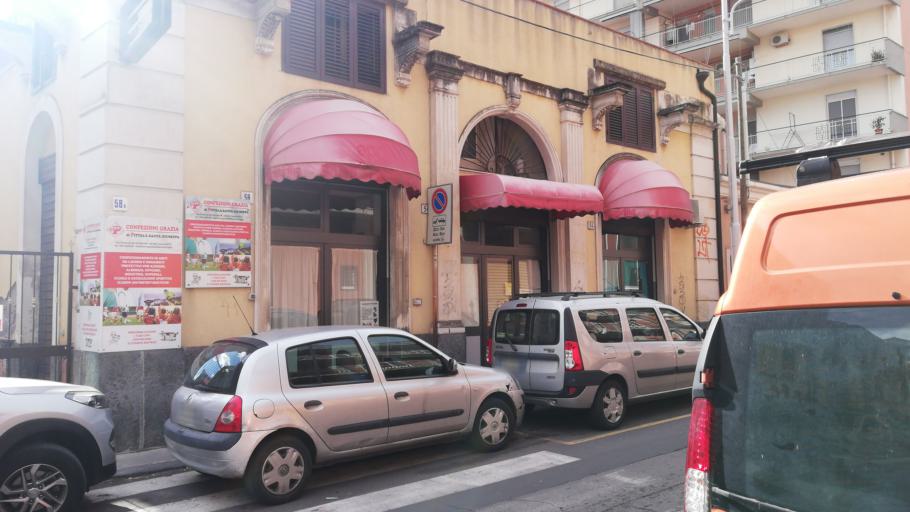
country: IT
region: Sicily
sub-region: Catania
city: Canalicchio
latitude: 37.5196
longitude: 15.0862
